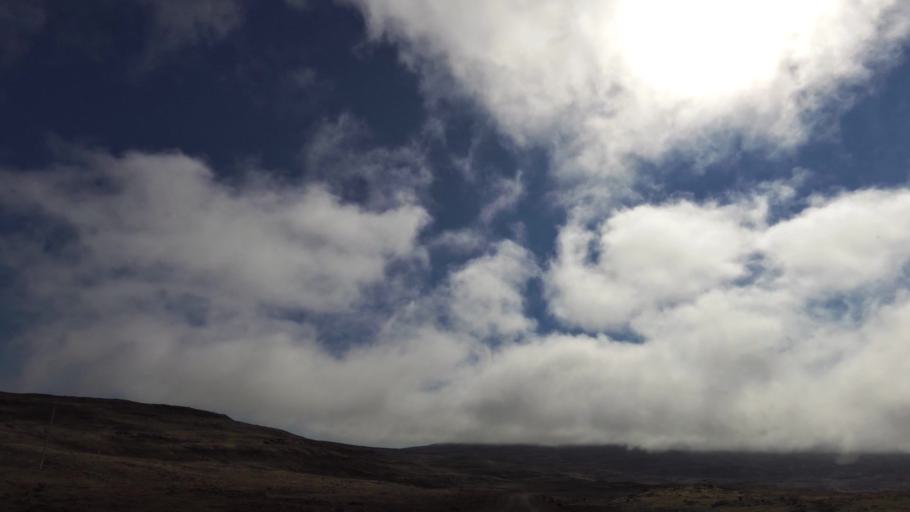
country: IS
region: West
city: Olafsvik
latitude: 65.5536
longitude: -24.2614
